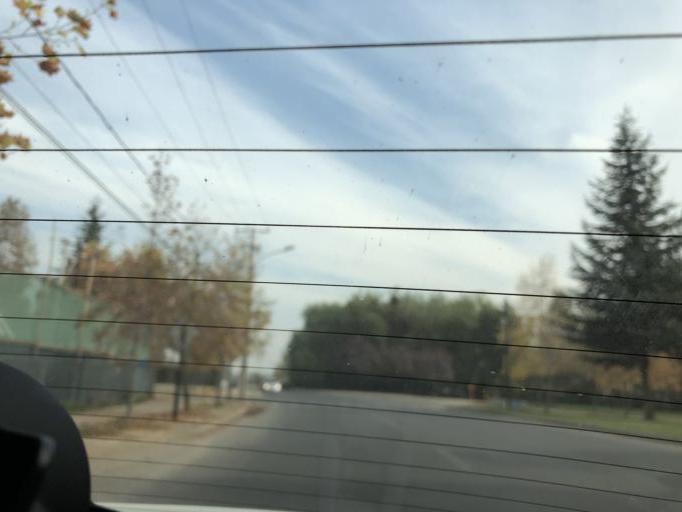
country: CL
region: Santiago Metropolitan
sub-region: Provincia de Cordillera
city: Puente Alto
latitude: -33.5518
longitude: -70.5533
